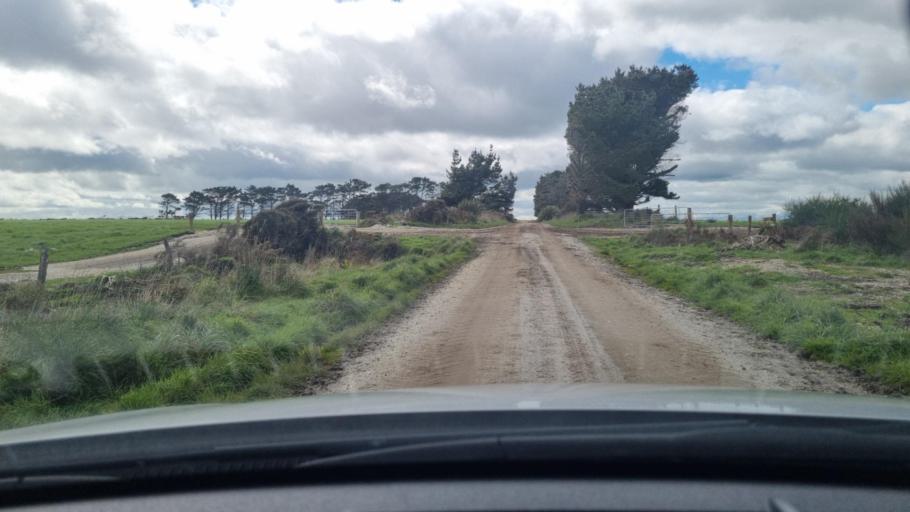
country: NZ
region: Southland
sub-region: Invercargill City
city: Bluff
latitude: -46.5690
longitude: 168.5004
